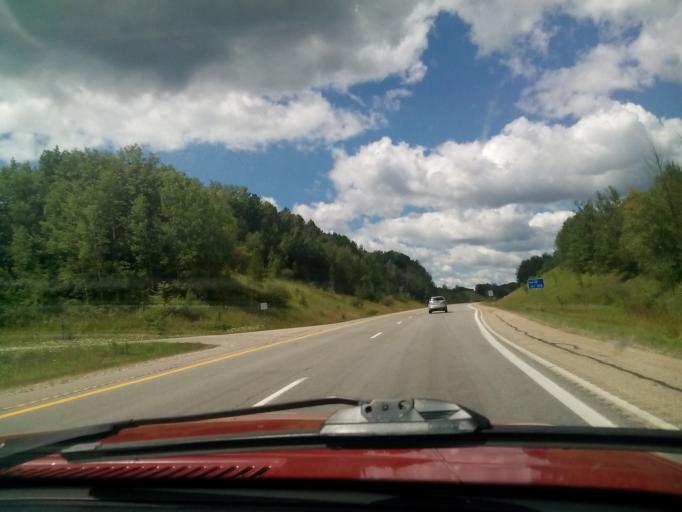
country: US
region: Michigan
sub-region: Ogemaw County
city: West Branch
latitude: 44.2635
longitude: -84.2654
